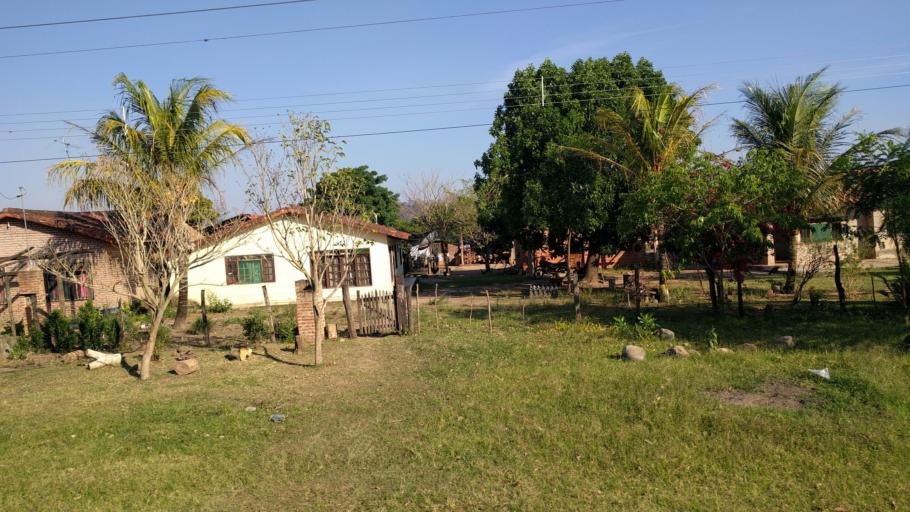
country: BO
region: Santa Cruz
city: Jorochito
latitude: -18.1482
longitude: -63.4865
